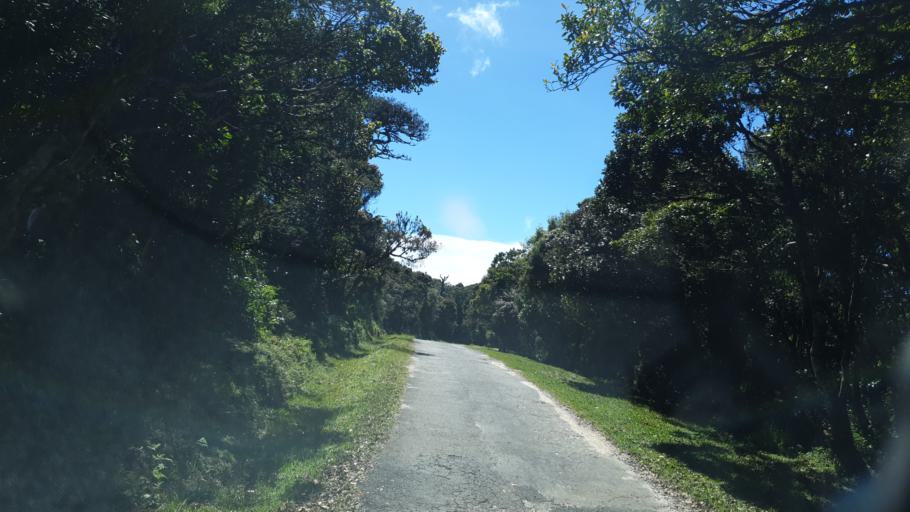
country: LK
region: Uva
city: Haputale
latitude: 6.8052
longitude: 80.8330
